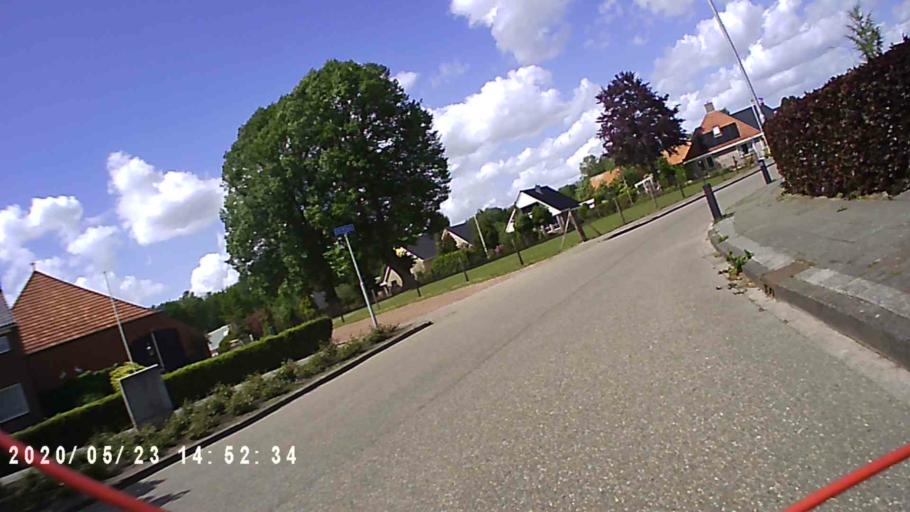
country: NL
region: Groningen
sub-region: Gemeente Delfzijl
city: Delfzijl
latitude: 53.2564
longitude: 6.9304
